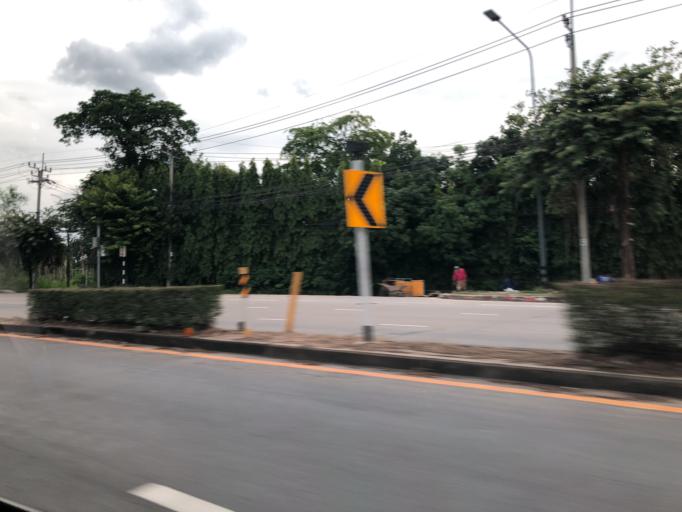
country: TH
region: Nonthaburi
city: Pak Kret
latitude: 13.9100
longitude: 100.5181
